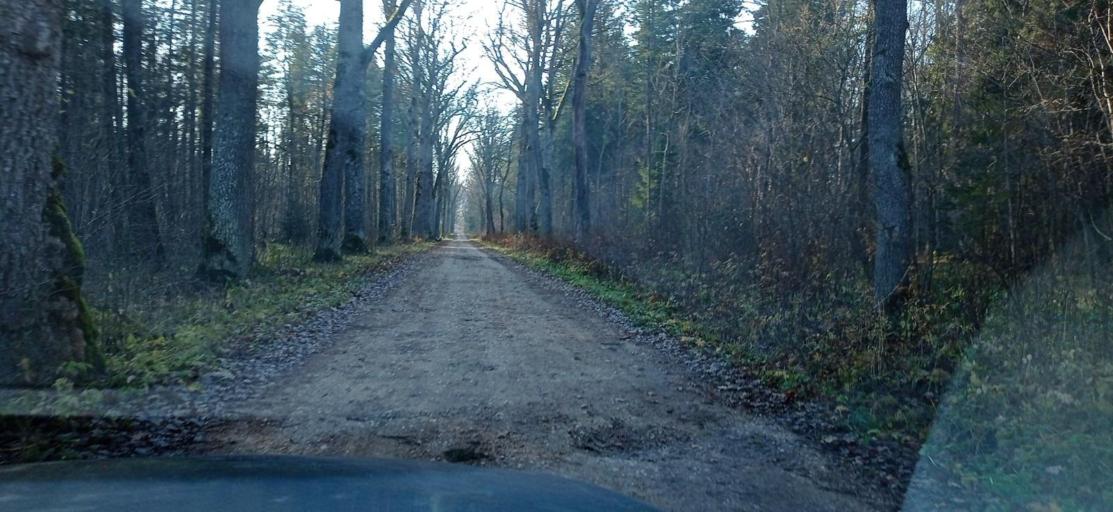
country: EE
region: Jogevamaa
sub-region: Tabivere vald
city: Tabivere
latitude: 58.6515
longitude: 26.5905
